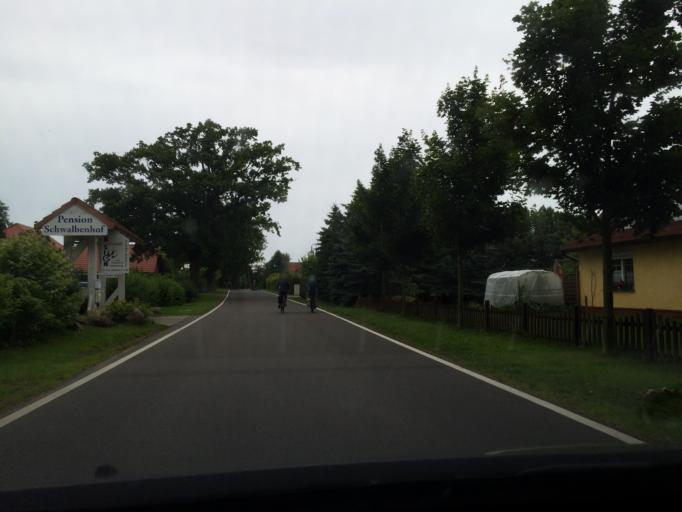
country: DE
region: Mecklenburg-Vorpommern
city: Prohn
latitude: 54.4137
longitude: 13.0150
